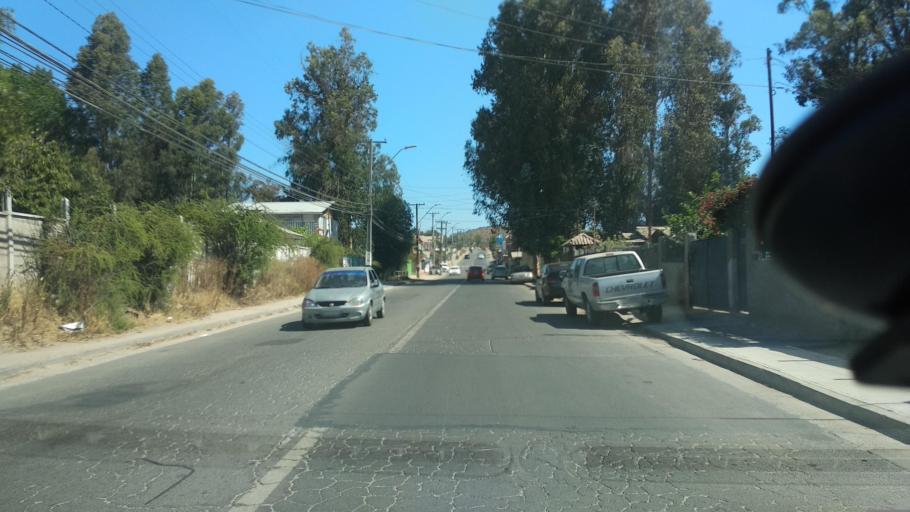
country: CL
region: Valparaiso
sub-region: Provincia de Marga Marga
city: Villa Alemana
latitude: -33.0630
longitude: -71.3711
